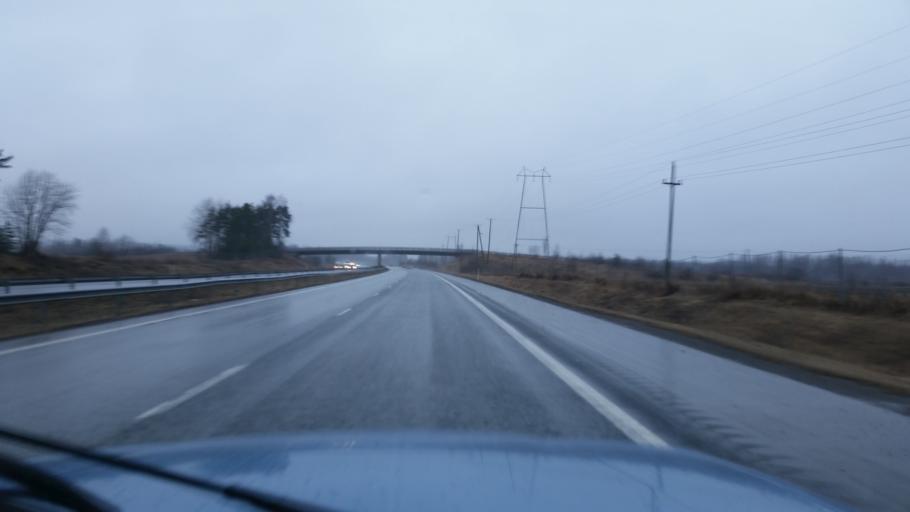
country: FI
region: Pirkanmaa
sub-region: Etelae-Pirkanmaa
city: Akaa
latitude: 61.1898
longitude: 23.8722
